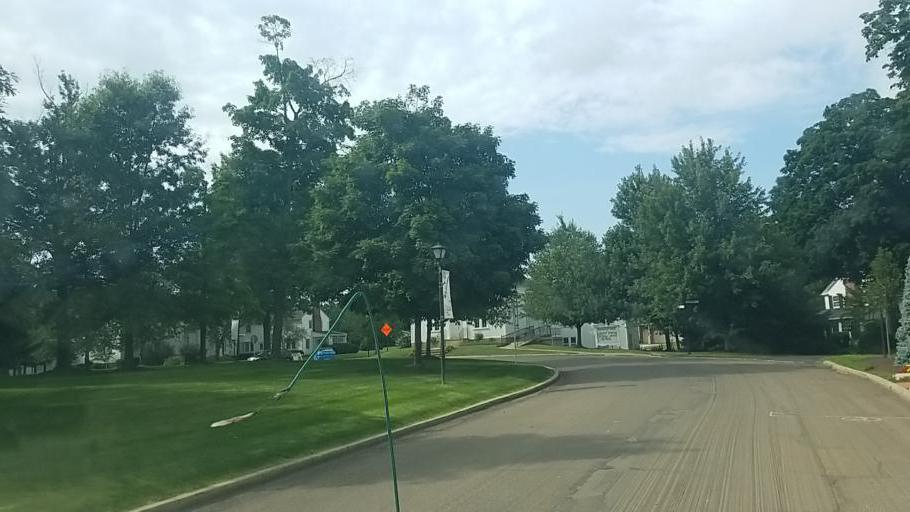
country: US
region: Ohio
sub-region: Medina County
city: Westfield Center
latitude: 41.0269
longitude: -81.9329
